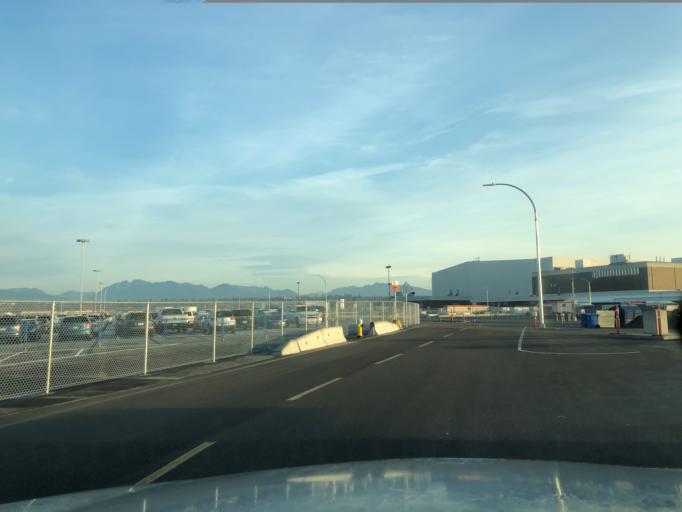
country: CA
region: British Columbia
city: Richmond
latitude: 49.1939
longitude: -123.1629
